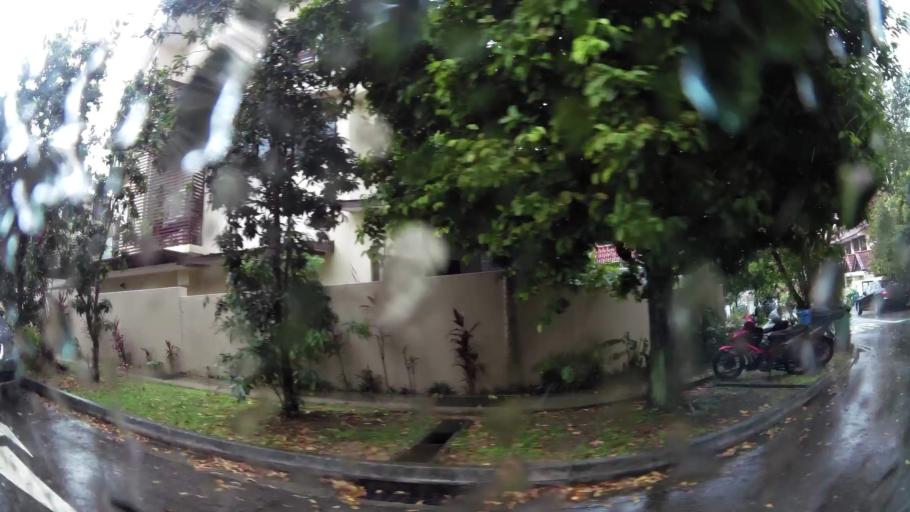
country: SG
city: Singapore
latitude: 1.3554
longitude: 103.8607
